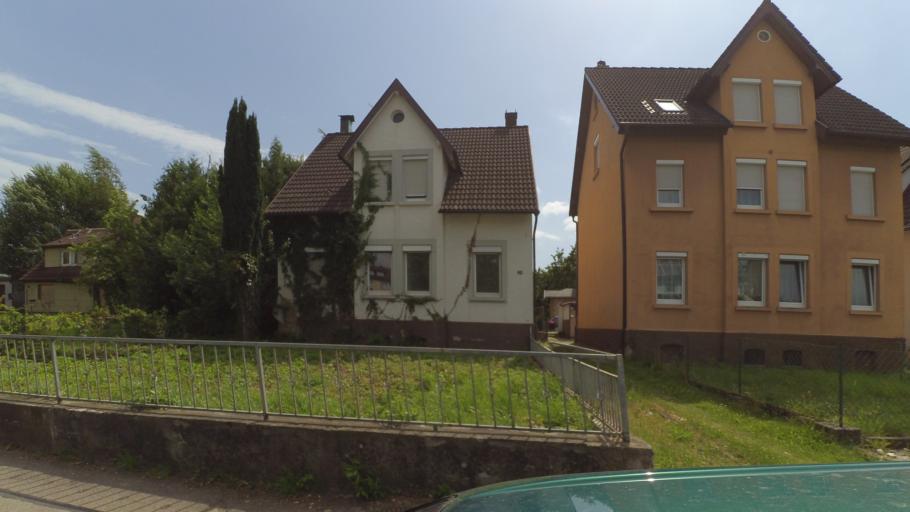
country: DE
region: Baden-Wuerttemberg
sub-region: Regierungsbezirk Stuttgart
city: Aalen
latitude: 48.8346
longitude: 10.1024
